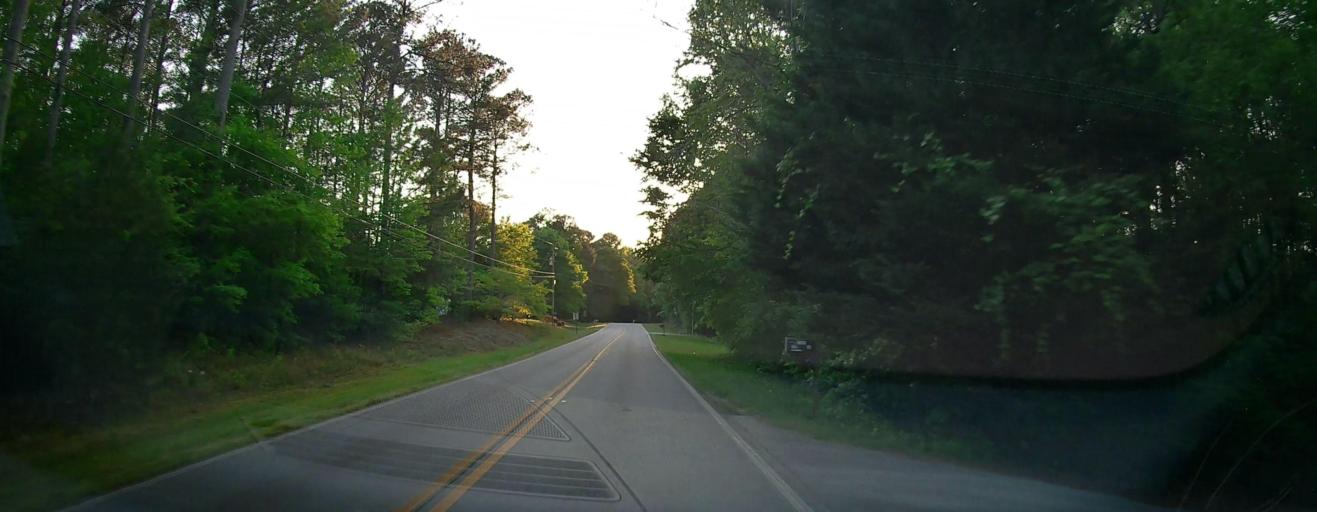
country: US
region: Georgia
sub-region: Henry County
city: Locust Grove
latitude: 33.4060
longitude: -84.1025
